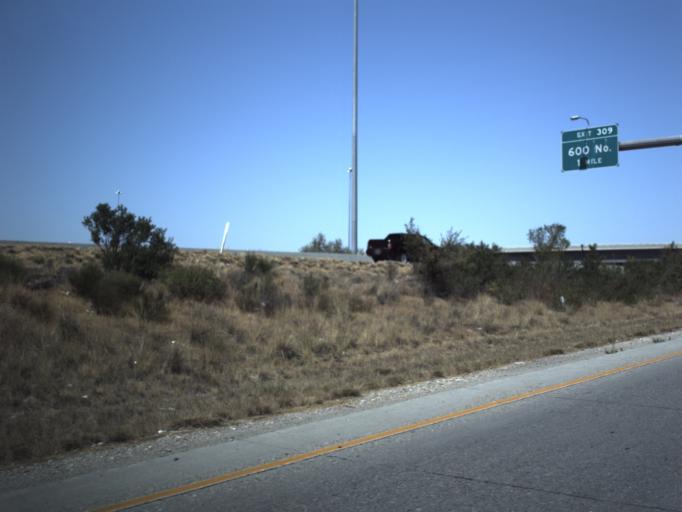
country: US
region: Utah
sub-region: Salt Lake County
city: Salt Lake City
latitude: 40.7621
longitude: -111.9137
